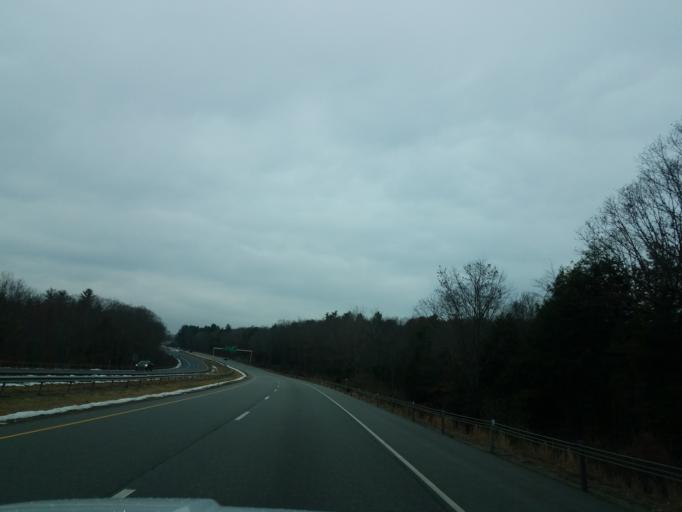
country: US
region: Connecticut
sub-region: Windham County
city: Danielson
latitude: 41.7843
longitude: -71.8719
